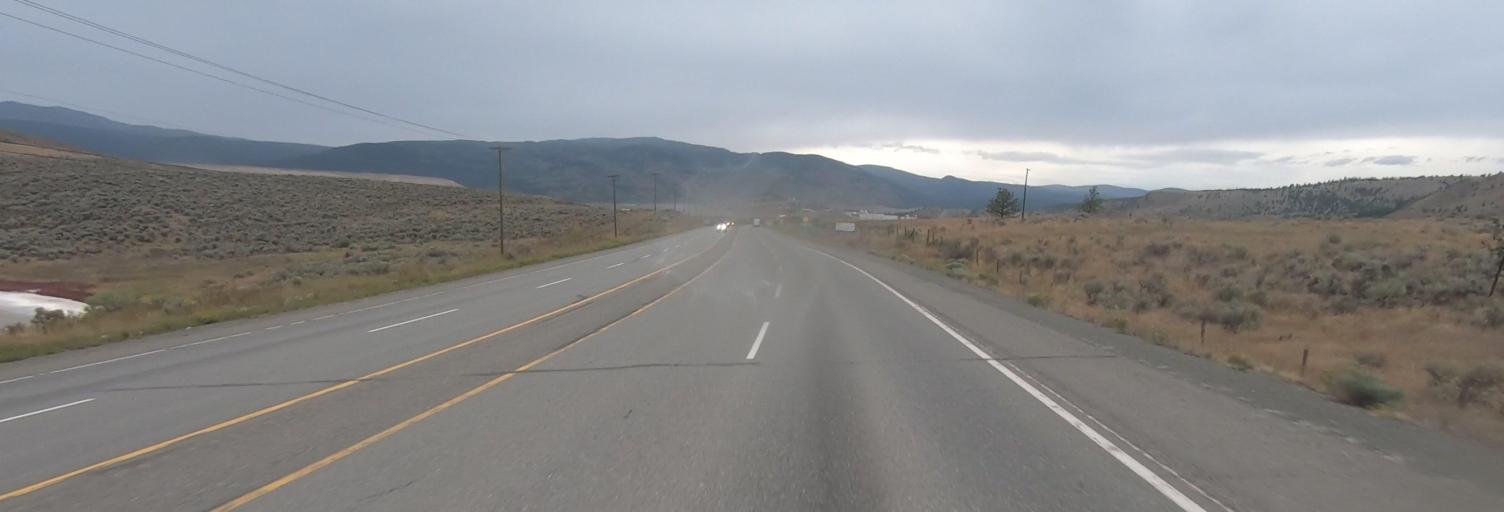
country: CA
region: British Columbia
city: Kamloops
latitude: 50.6692
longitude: -120.4843
